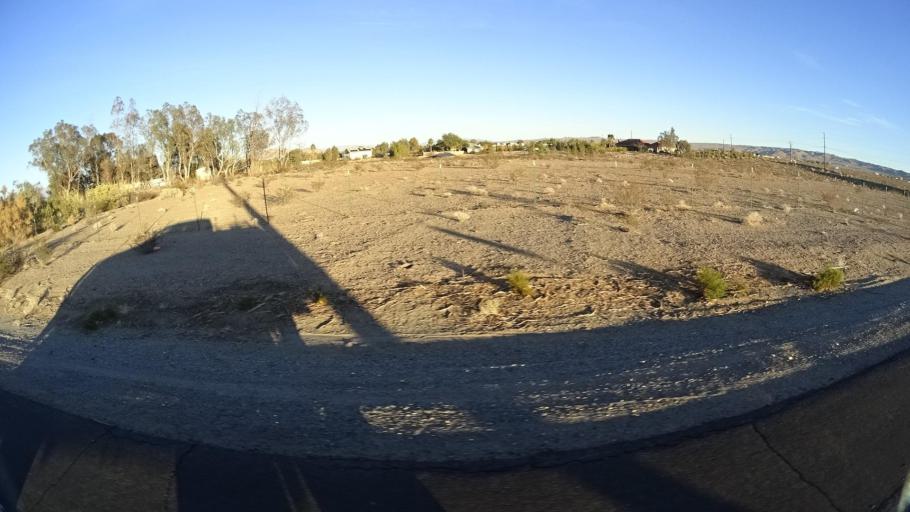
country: US
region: California
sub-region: Kern County
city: China Lake Acres
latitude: 35.6240
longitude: -117.7230
